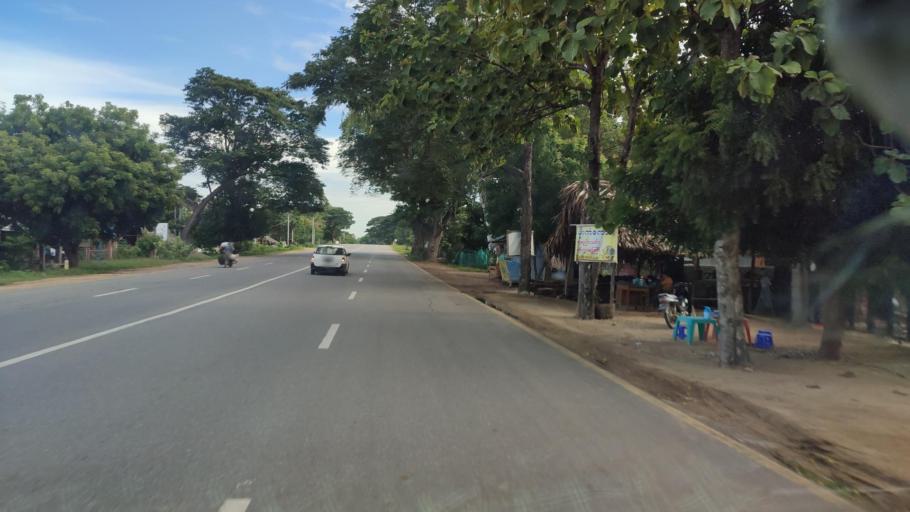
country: MM
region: Mandalay
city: Yamethin
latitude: 20.2088
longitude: 96.1810
